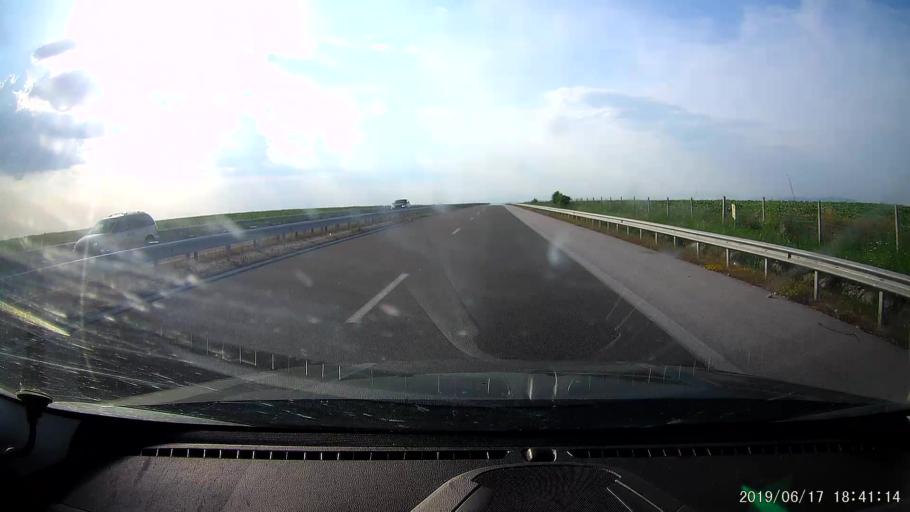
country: BG
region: Stara Zagora
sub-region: Obshtina Chirpan
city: Chirpan
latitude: 42.1684
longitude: 25.2595
